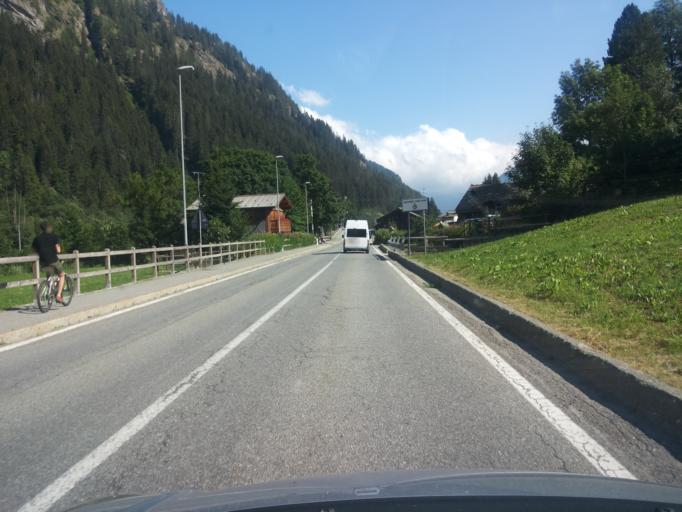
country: IT
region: Aosta Valley
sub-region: Valle d'Aosta
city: Gressoney-Saint-Jean
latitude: 45.7840
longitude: 7.8222
